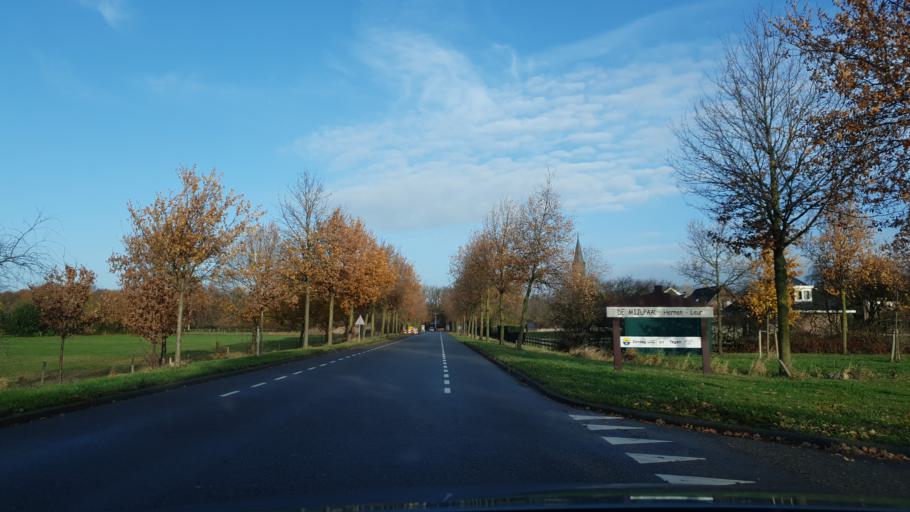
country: NL
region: Gelderland
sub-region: Gemeente Wijchen
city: Bergharen
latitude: 51.8314
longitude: 5.6794
